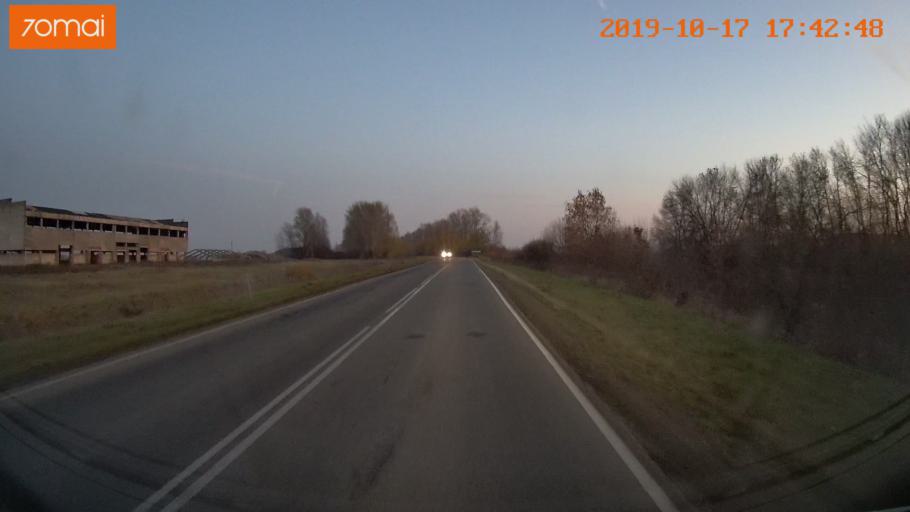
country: RU
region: Tula
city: Yepifan'
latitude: 53.7668
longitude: 38.6512
